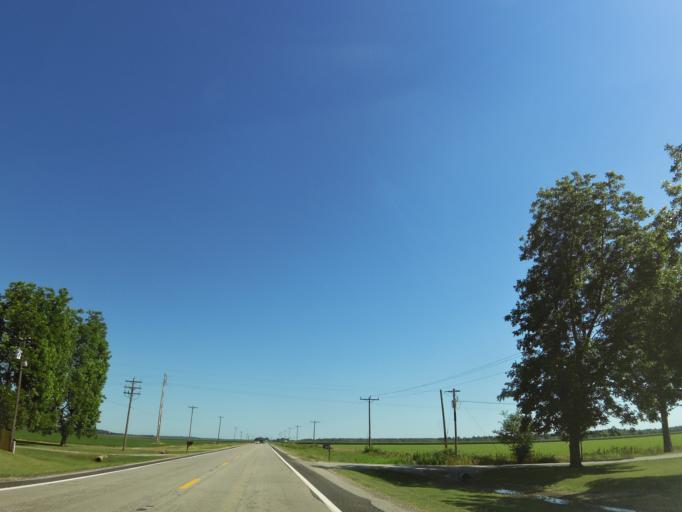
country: US
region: Arkansas
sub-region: Clay County
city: Piggott
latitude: 36.3959
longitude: -90.1483
